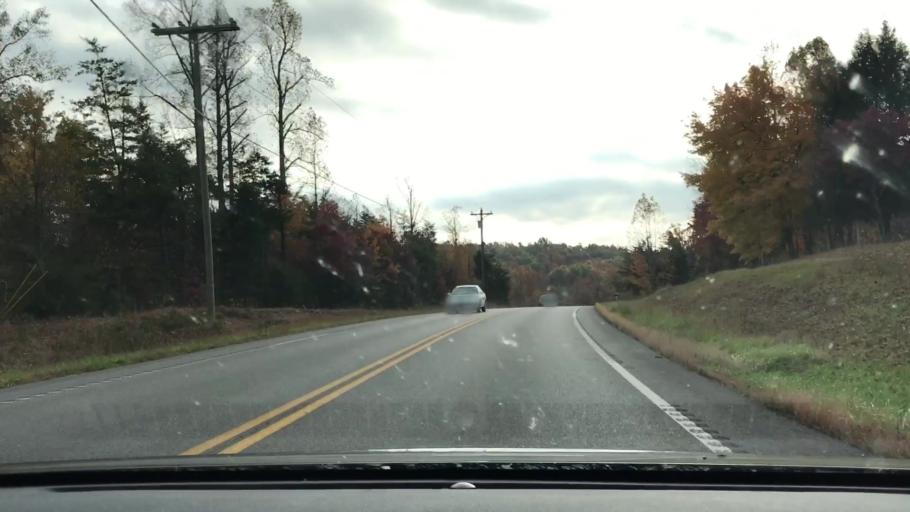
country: US
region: Tennessee
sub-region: Putnam County
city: Monterey
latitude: 36.1322
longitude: -85.2093
